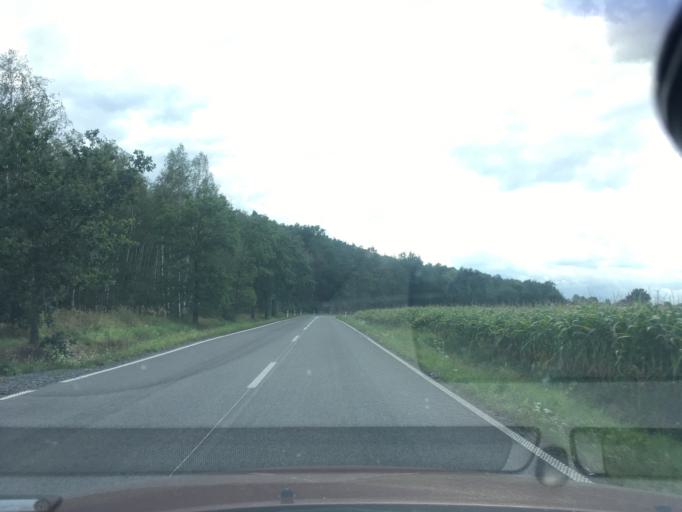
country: PL
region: Lower Silesian Voivodeship
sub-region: Powiat zgorzelecki
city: Piensk
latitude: 51.2216
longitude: 15.0253
